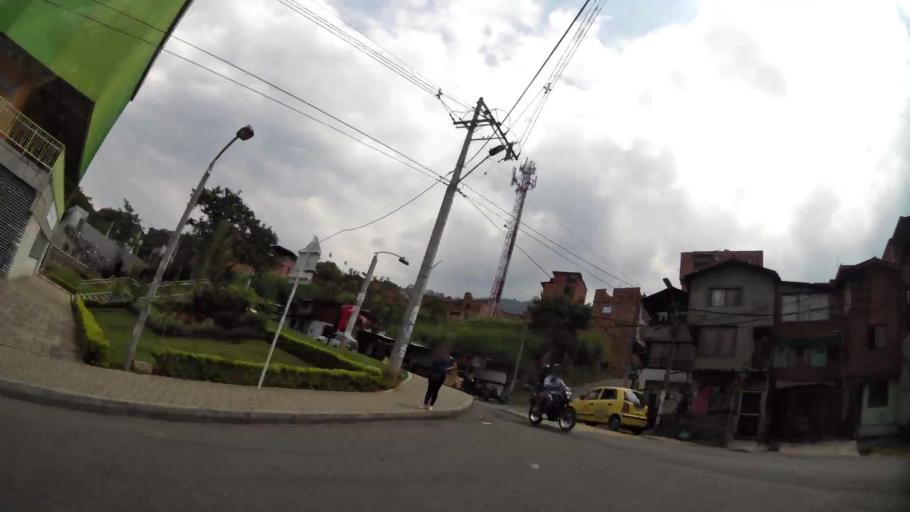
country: CO
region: Antioquia
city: Medellin
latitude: 6.2686
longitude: -75.5492
